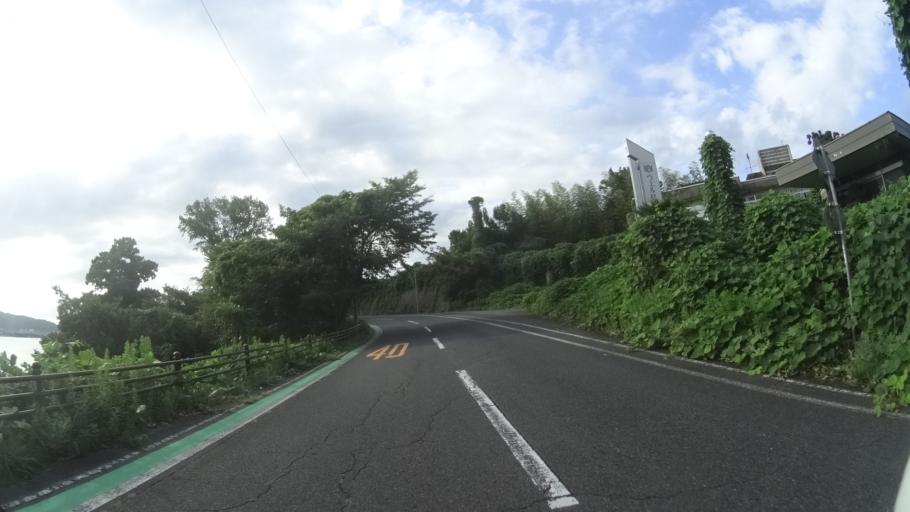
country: JP
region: Tottori
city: Kurayoshi
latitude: 35.4814
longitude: 133.8965
